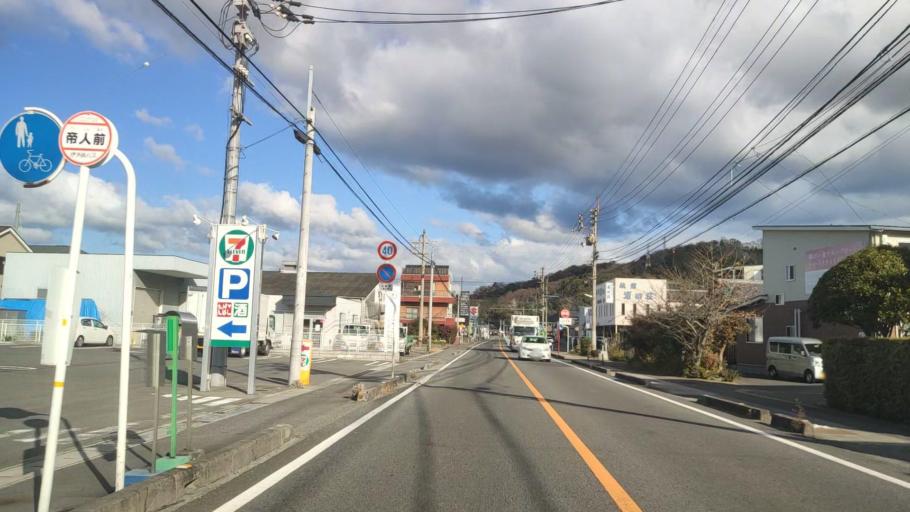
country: JP
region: Ehime
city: Masaki-cho
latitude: 33.8358
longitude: 132.7092
